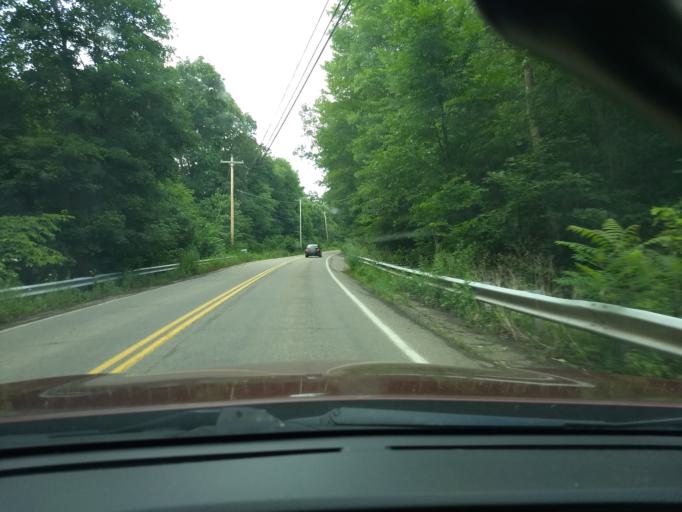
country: US
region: Pennsylvania
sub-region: Butler County
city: Cranberry Township
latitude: 40.6481
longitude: -80.1236
